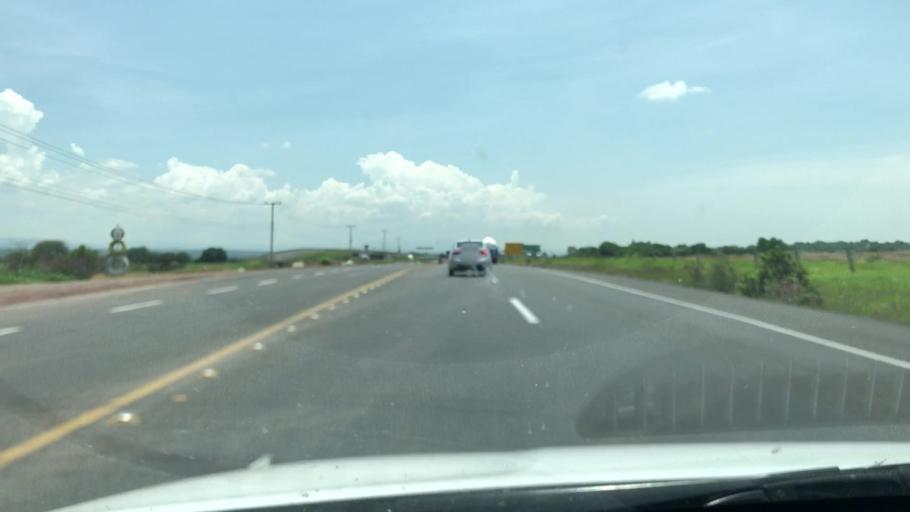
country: MX
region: Jalisco
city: Degollado
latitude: 20.3652
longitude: -102.1347
